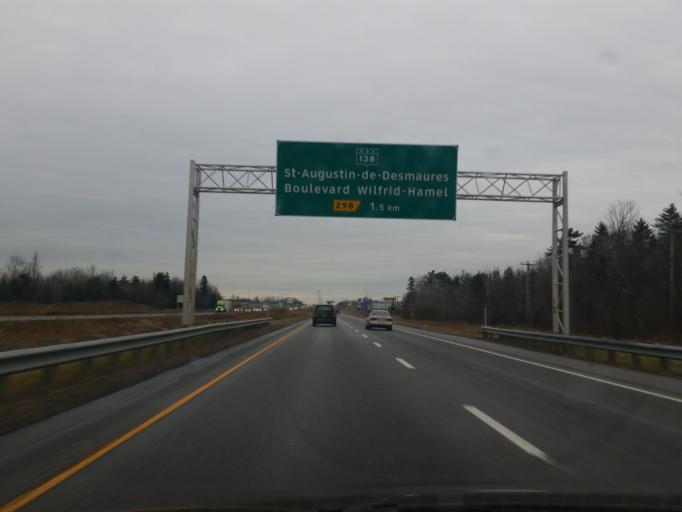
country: CA
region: Quebec
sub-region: Capitale-Nationale
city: Saint-Augustin-de-Desmaures
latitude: 46.7611
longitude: -71.4475
